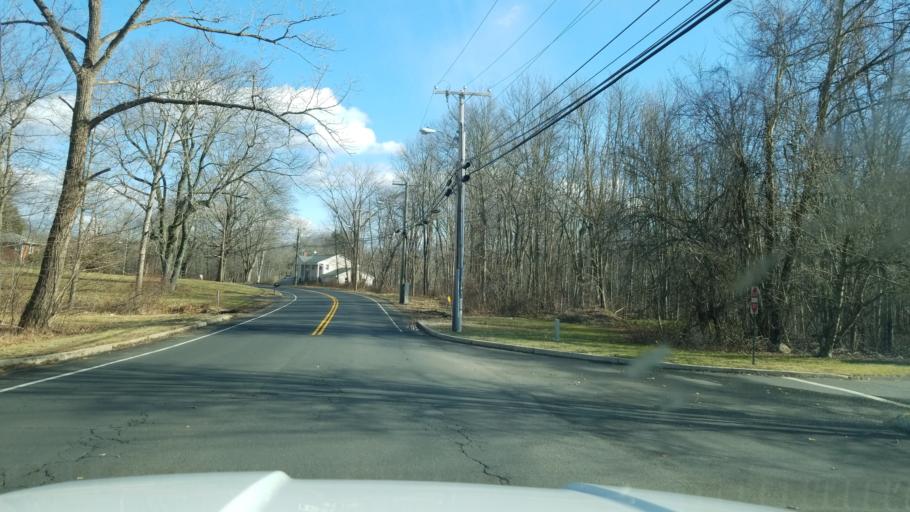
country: US
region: Connecticut
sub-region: Middlesex County
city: Middletown
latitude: 41.5628
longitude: -72.7060
